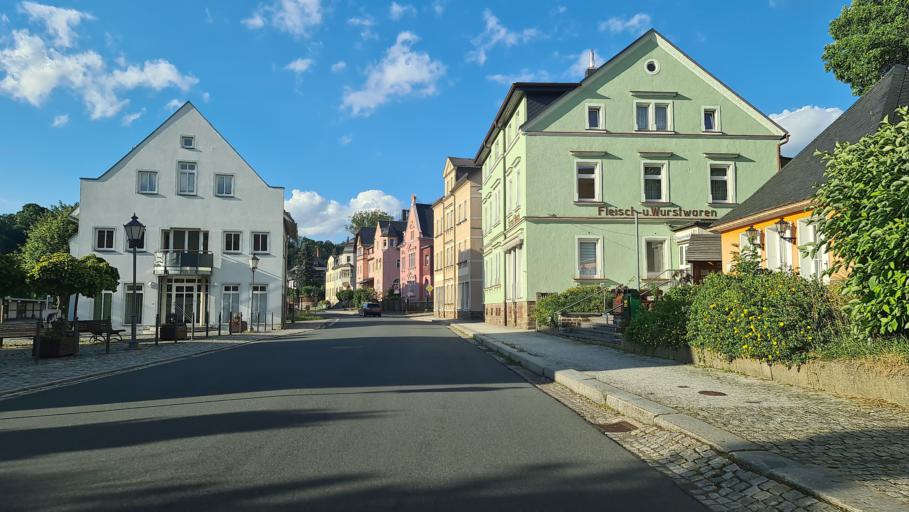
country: DE
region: Saxony
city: Neuhausen
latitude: 50.6747
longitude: 13.4659
